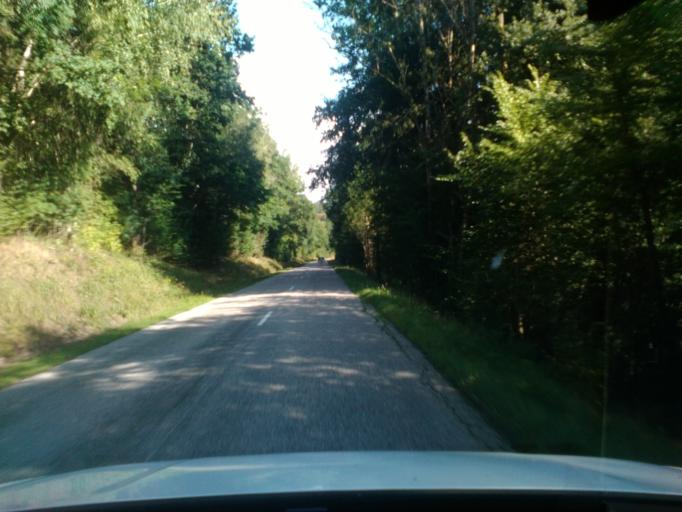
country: FR
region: Lorraine
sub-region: Departement des Vosges
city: Taintrux
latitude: 48.2359
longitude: 6.8997
